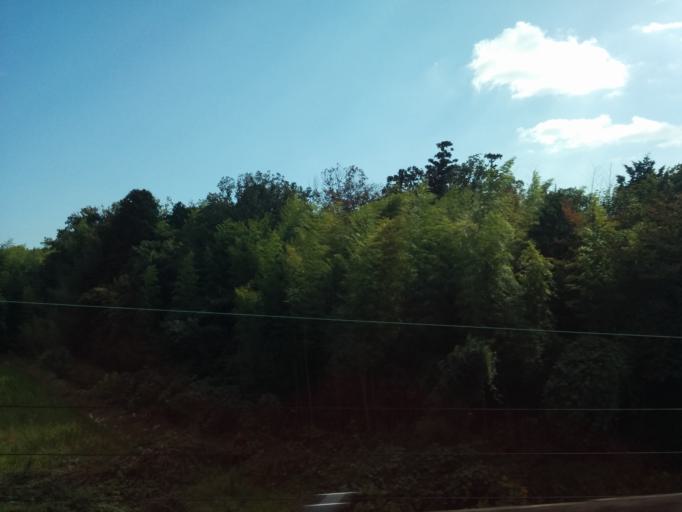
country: JP
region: Shiga Prefecture
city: Kusatsu
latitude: 34.9784
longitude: 135.9370
